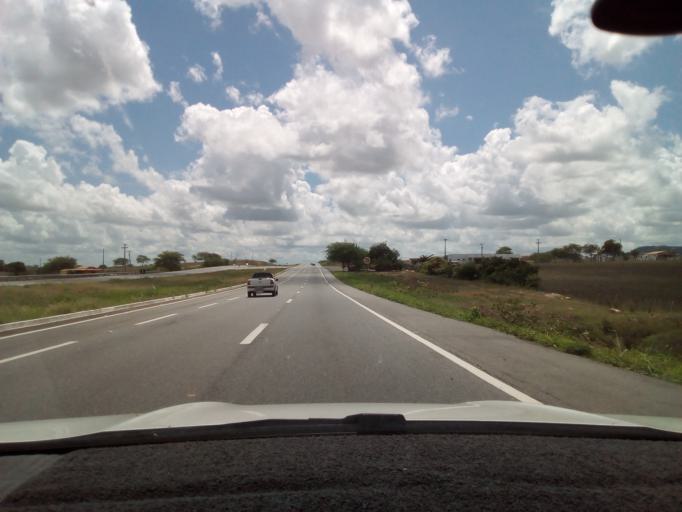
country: BR
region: Paraiba
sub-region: Mogeiro
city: Mogeiro
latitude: -7.2009
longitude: -35.4949
